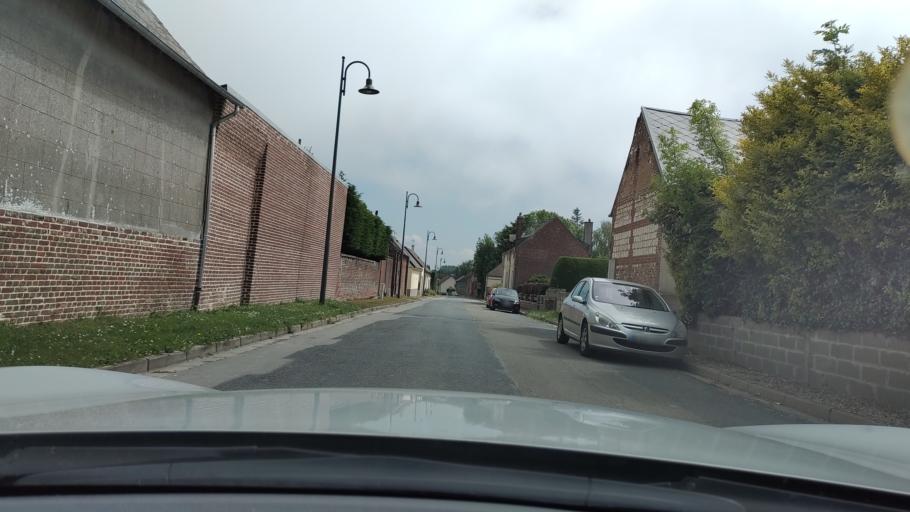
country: FR
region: Picardie
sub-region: Departement de la Somme
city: Ault
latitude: 50.0772
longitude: 1.4568
